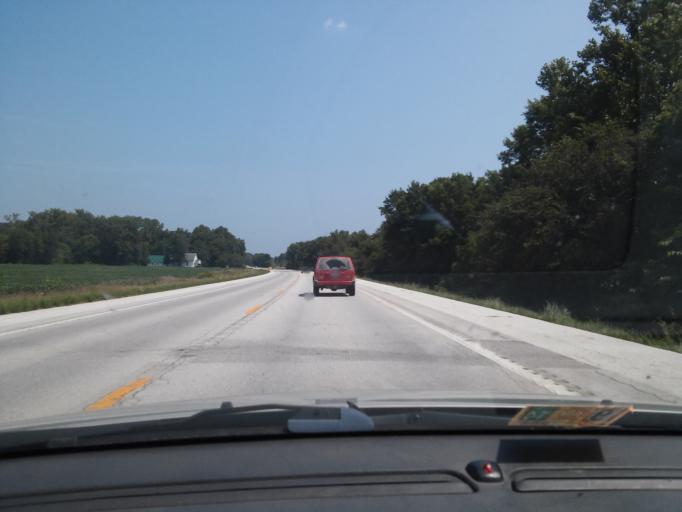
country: US
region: Missouri
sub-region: Pike County
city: Louisiana
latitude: 39.3907
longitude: -91.1168
